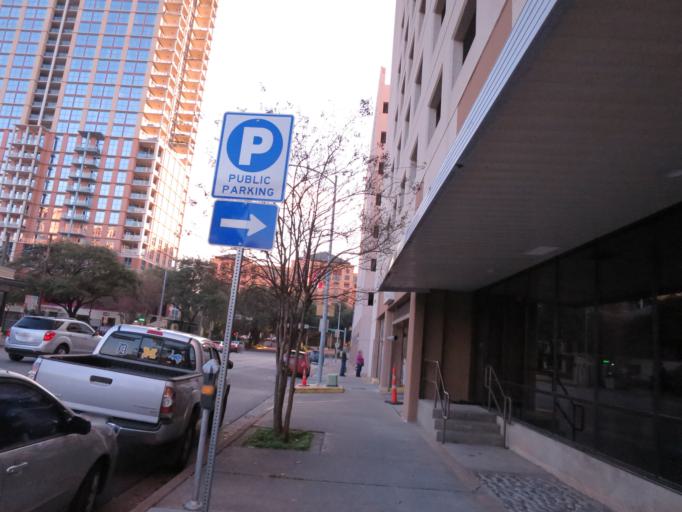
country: US
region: Texas
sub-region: Travis County
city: Austin
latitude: 30.2636
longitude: -97.7420
